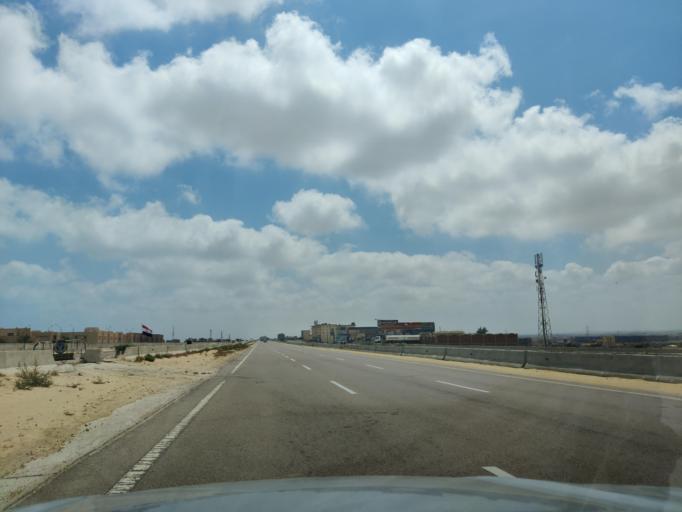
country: EG
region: Muhafazat Matruh
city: Al `Alamayn
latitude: 30.8185
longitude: 29.1549
